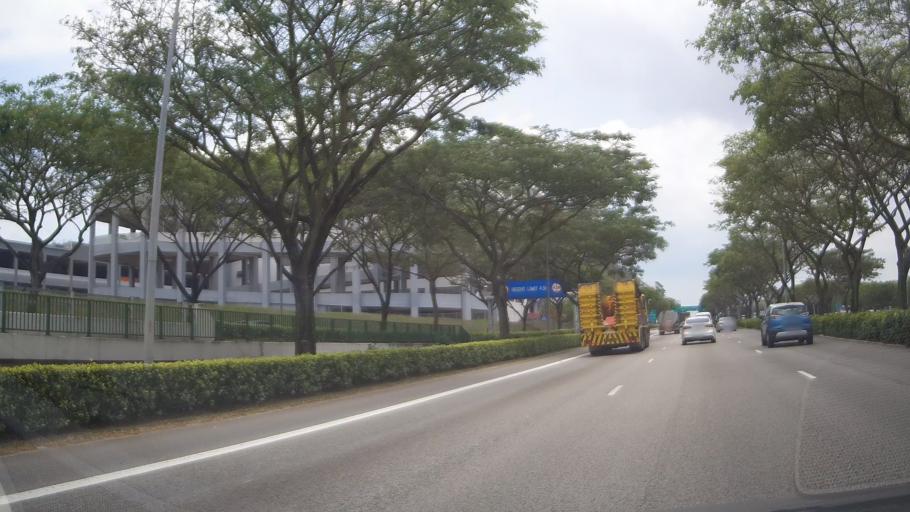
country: SG
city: Singapore
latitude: 1.3742
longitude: 103.9093
